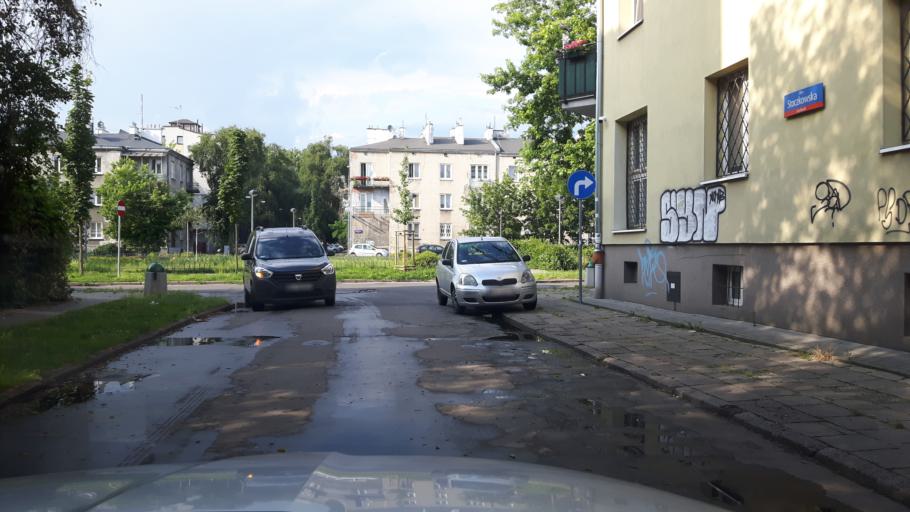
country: PL
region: Masovian Voivodeship
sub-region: Warszawa
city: Praga Poludnie
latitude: 52.2424
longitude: 21.1055
